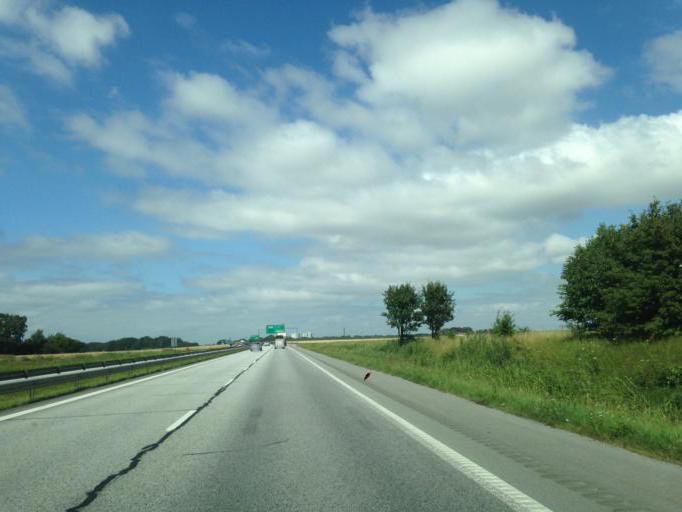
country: SE
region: Skane
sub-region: Malmo
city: Tygelsjo
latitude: 55.5318
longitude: 13.0073
